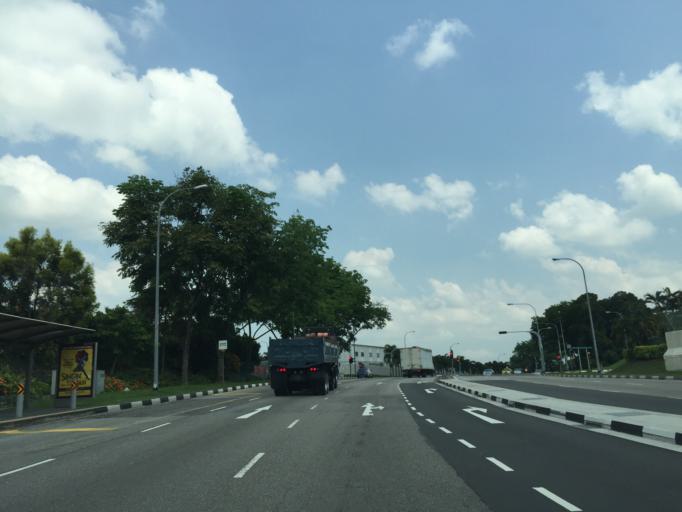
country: MY
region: Johor
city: Johor Bahru
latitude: 1.4293
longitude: 103.7668
